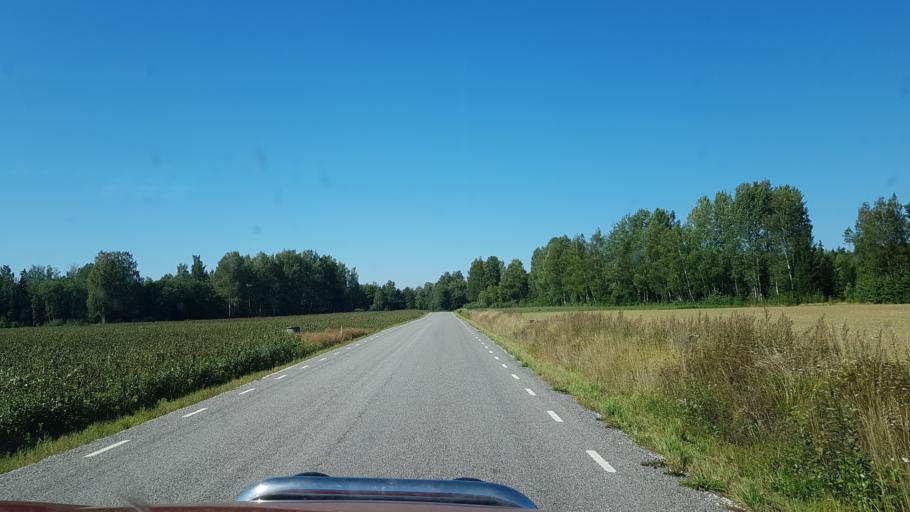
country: EE
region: Polvamaa
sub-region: Polva linn
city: Polva
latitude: 58.2101
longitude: 27.2380
